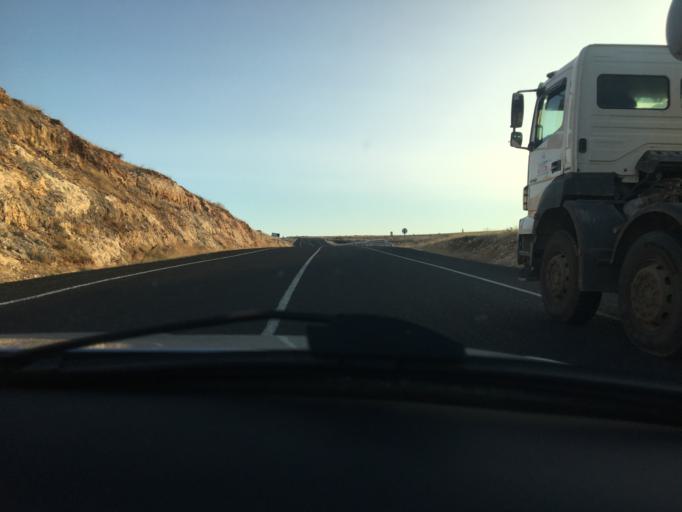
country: TR
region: Sanliurfa
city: Bogurtlen
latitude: 37.1832
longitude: 37.9758
